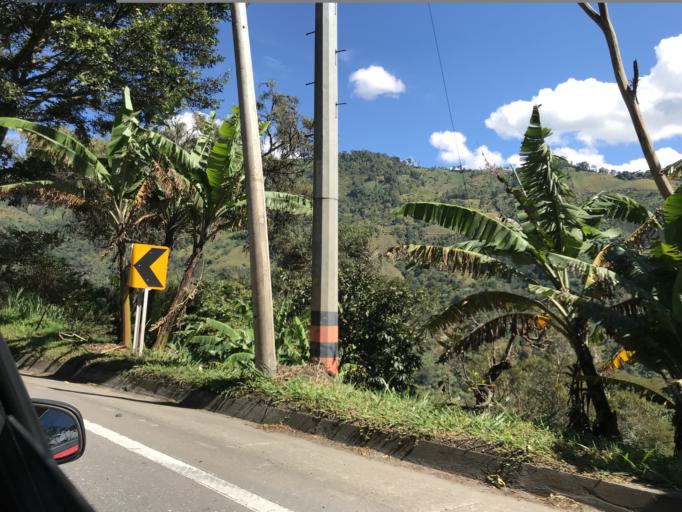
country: CO
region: Tolima
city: Cajamarca
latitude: 4.4395
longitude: -75.4026
